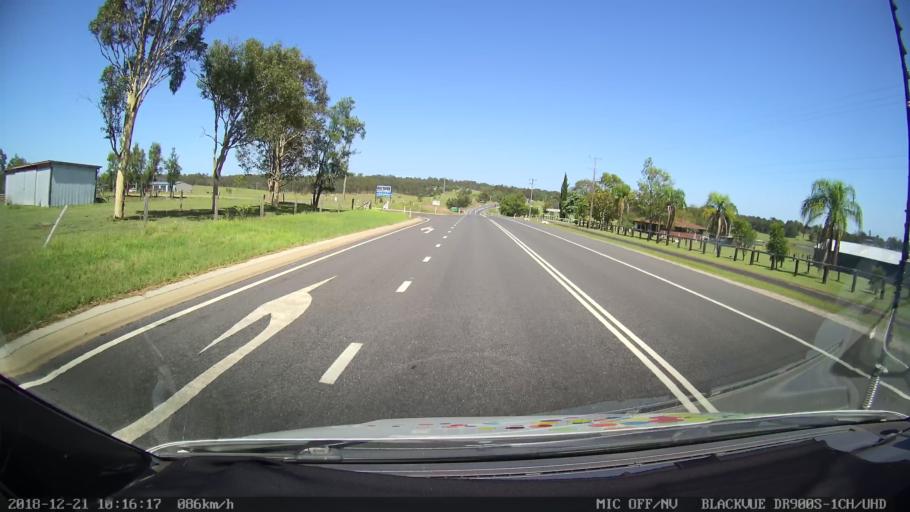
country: AU
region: New South Wales
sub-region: Clarence Valley
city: South Grafton
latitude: -29.6847
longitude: 152.8874
